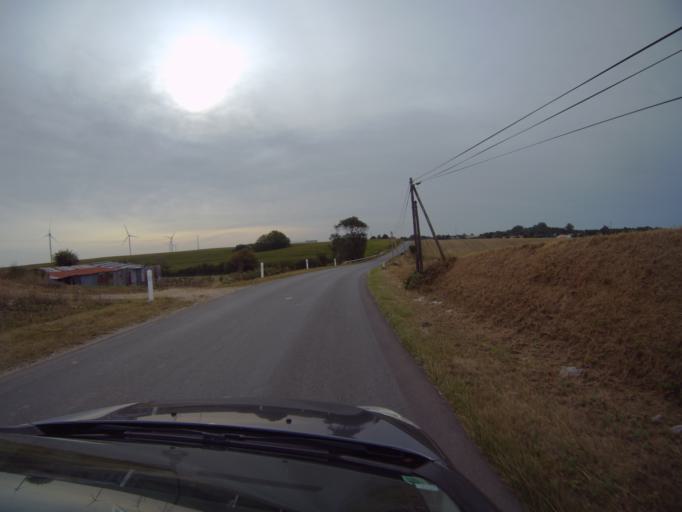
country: FR
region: Pays de la Loire
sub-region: Departement de la Vendee
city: Longeville-sur-Mer
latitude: 46.4176
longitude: -1.4584
